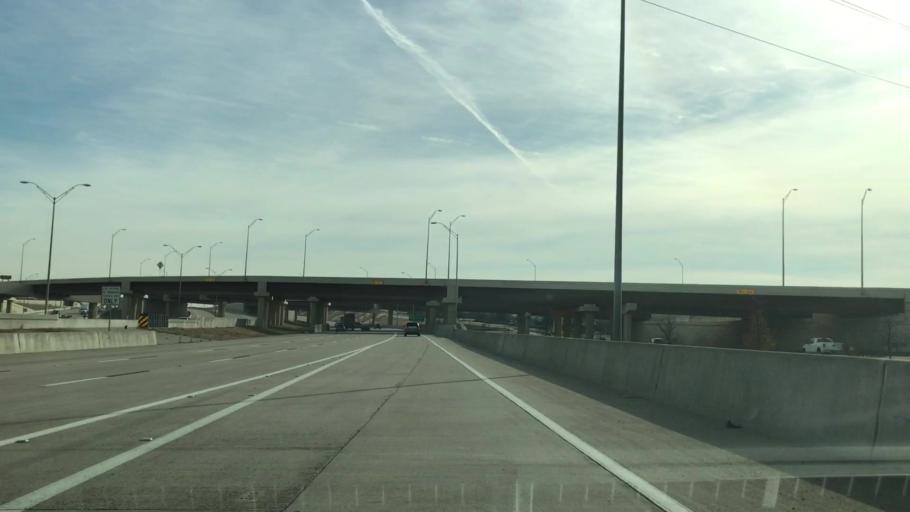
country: US
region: Texas
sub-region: Tarrant County
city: Grapevine
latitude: 32.9238
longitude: -97.0864
